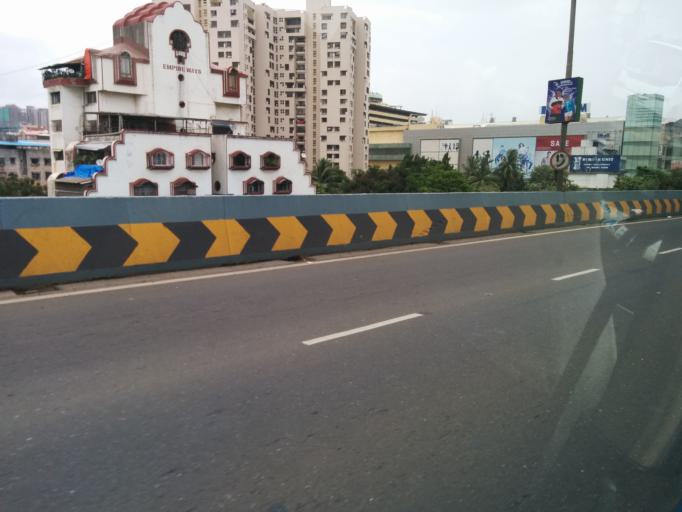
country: IN
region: Maharashtra
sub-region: Thane
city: Thane
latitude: 19.2006
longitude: 72.9645
